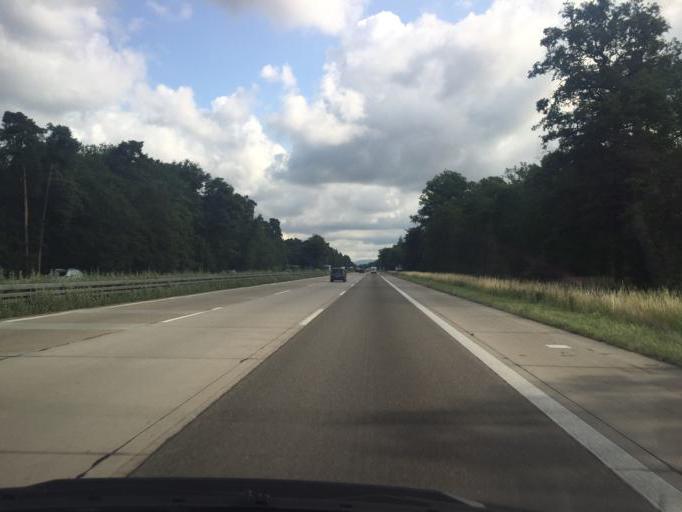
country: DE
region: Baden-Wuerttemberg
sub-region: Karlsruhe Region
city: Forst
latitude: 49.1951
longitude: 8.5894
